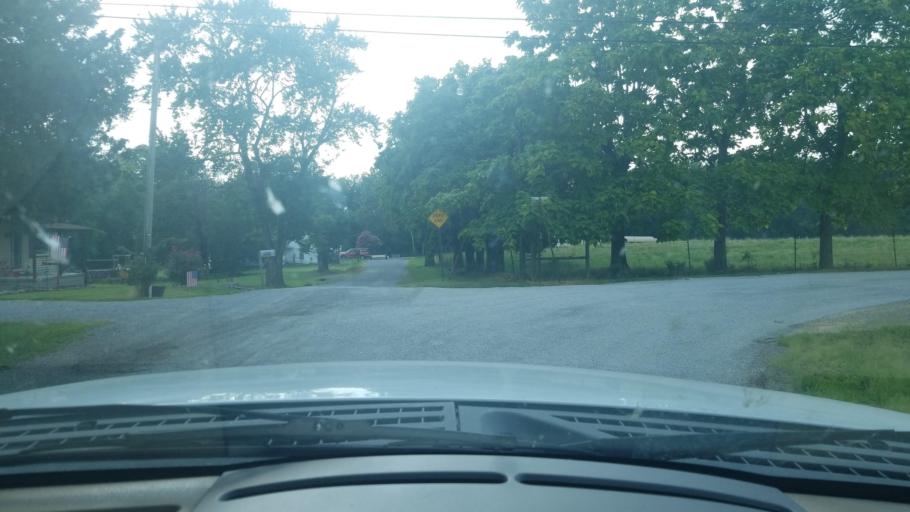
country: US
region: Illinois
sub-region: Saline County
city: Eldorado
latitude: 37.8270
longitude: -88.4383
